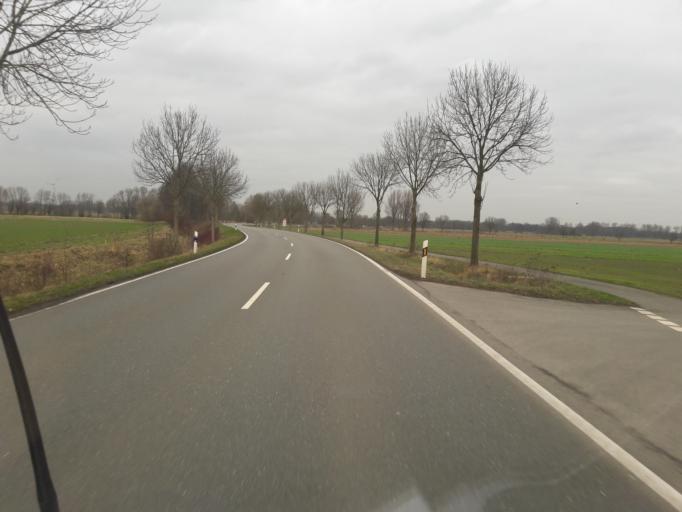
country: DE
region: North Rhine-Westphalia
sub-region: Regierungsbezirk Detmold
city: Hille
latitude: 52.2939
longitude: 8.8006
